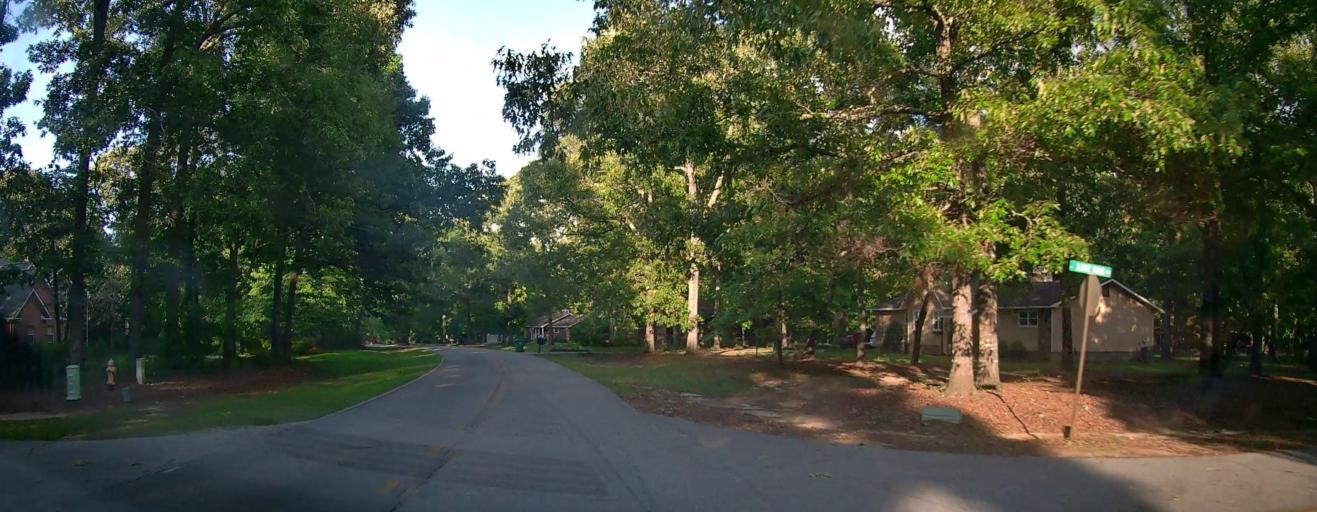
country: US
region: Georgia
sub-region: Peach County
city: Byron
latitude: 32.6343
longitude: -83.7513
